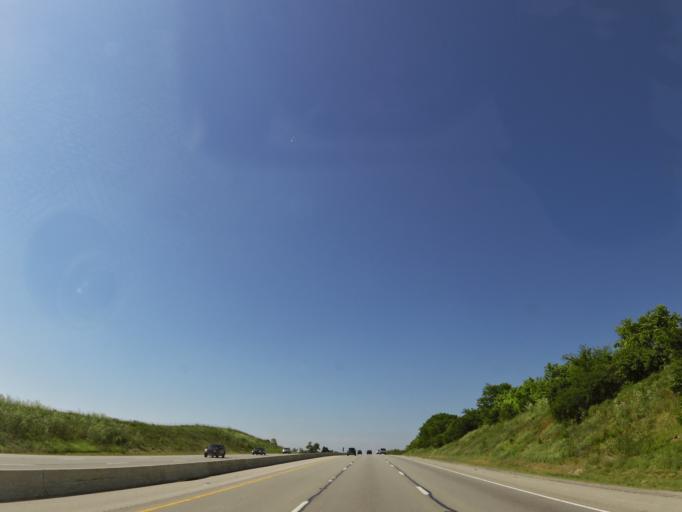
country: US
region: Kentucky
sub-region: Madison County
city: Berea
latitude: 37.6412
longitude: -84.3153
